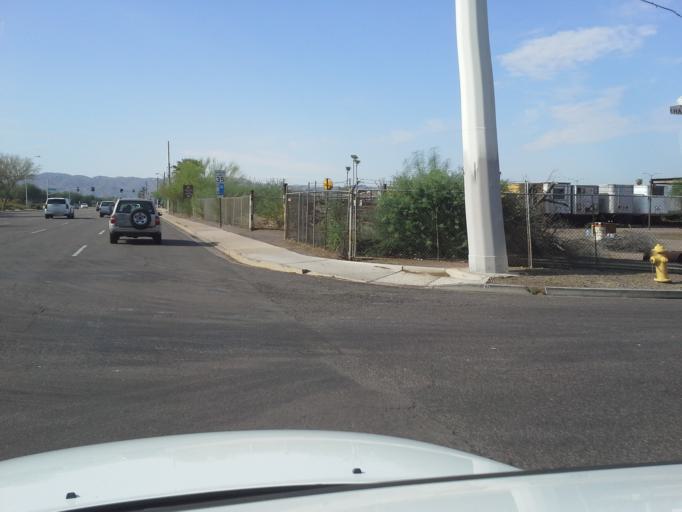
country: US
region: Arizona
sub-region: Maricopa County
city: Phoenix
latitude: 33.4392
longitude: -112.0479
